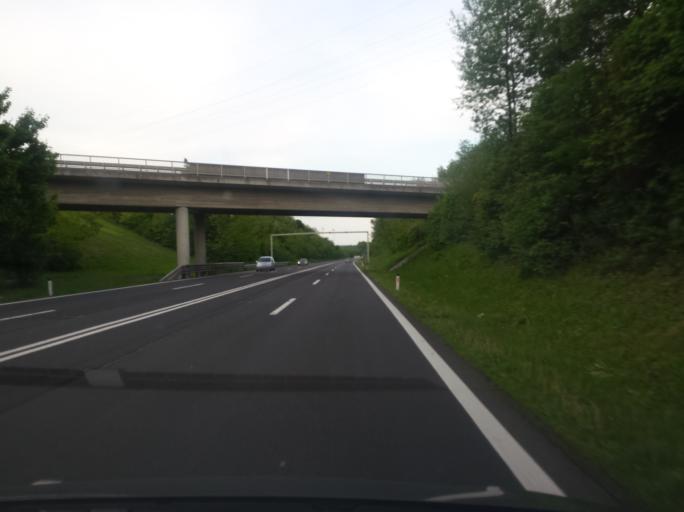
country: AT
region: Burgenland
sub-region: Politischer Bezirk Mattersburg
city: Mattersburg
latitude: 47.7448
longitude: 16.3809
